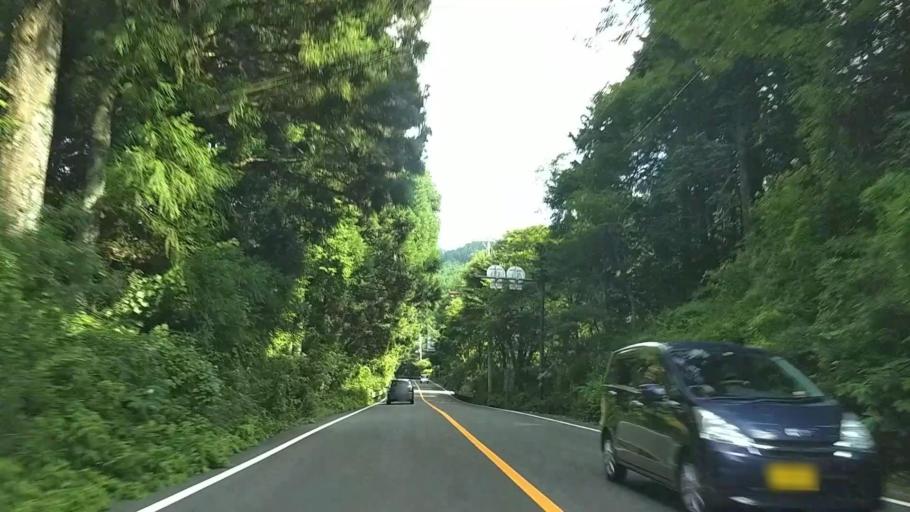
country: JP
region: Kanagawa
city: Hakone
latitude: 35.1878
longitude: 139.0181
